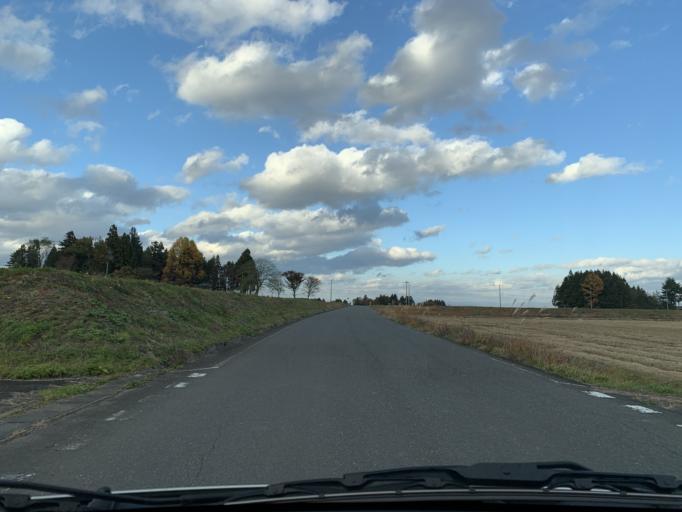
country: JP
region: Iwate
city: Mizusawa
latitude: 39.1055
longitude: 141.0217
